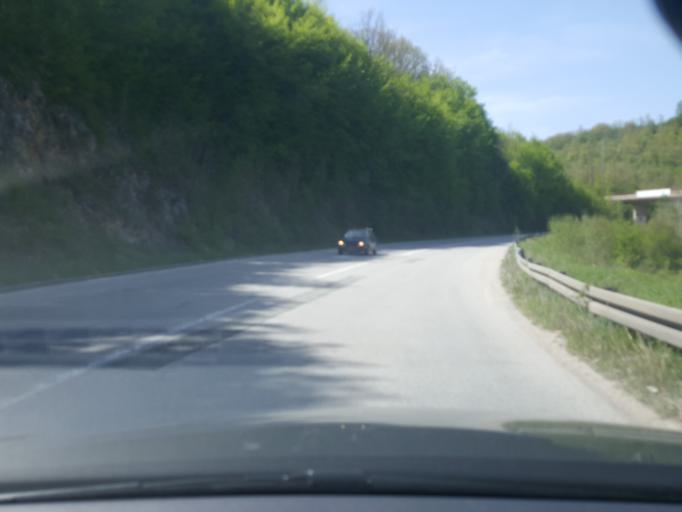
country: RS
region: Central Serbia
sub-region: Zlatiborski Okrug
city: Cajetina
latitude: 43.7848
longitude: 19.7355
